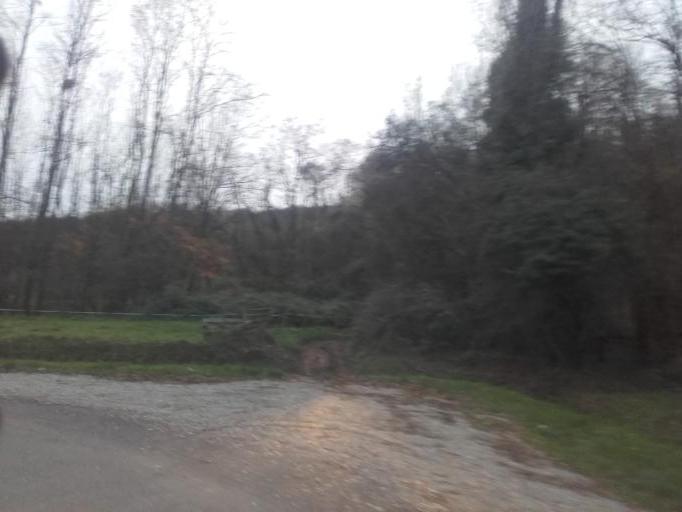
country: FR
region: Bourgogne
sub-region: Departement de Saone-et-Loire
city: Mellecey
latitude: 46.8339
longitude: 4.6904
